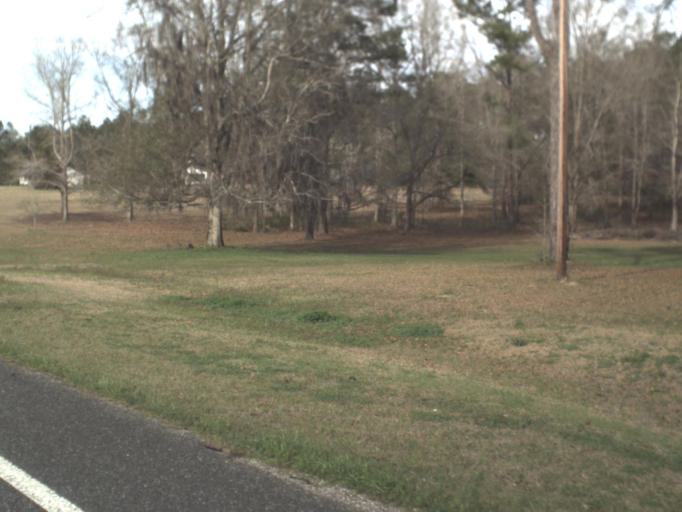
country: US
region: Florida
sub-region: Jefferson County
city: Monticello
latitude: 30.6096
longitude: -83.8721
